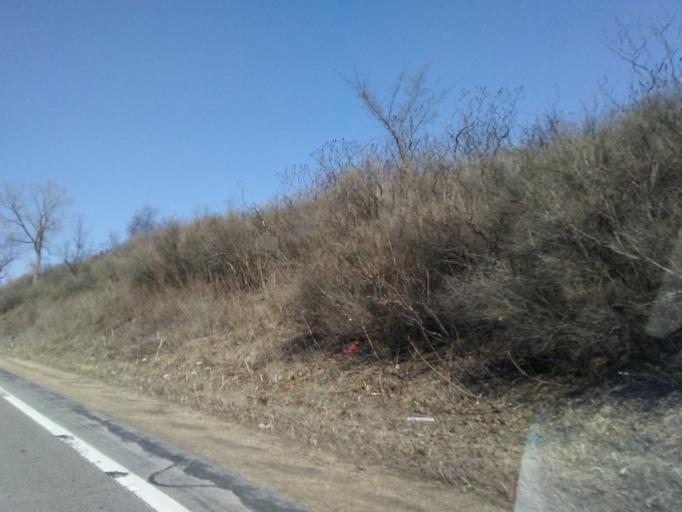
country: US
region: Wisconsin
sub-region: Vernon County
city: Viroqua
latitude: 43.5407
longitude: -90.8790
